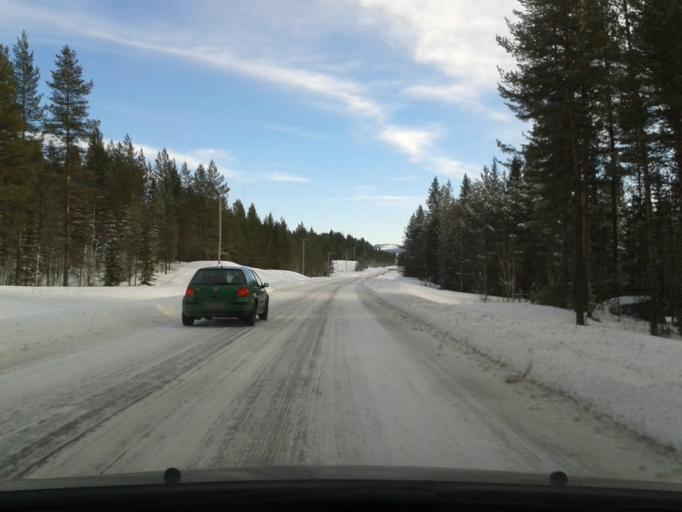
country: SE
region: Vaesterbotten
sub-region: Asele Kommun
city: Asele
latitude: 64.3549
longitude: 16.9779
